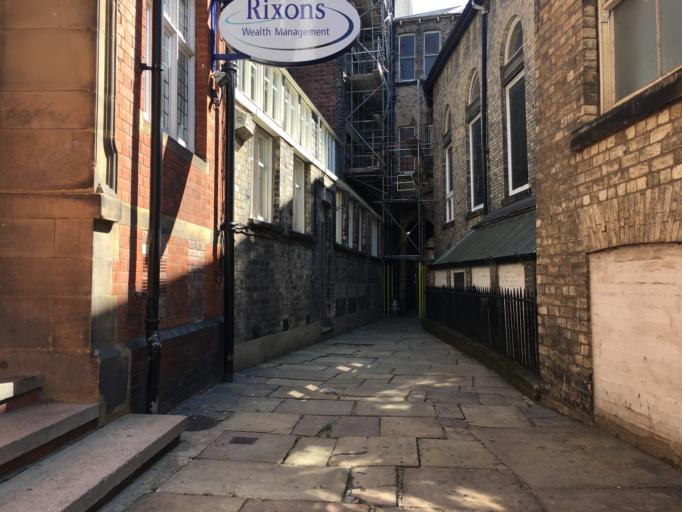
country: GB
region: England
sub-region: City of Kingston upon Hull
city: Hull
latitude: 53.7436
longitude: -0.3335
